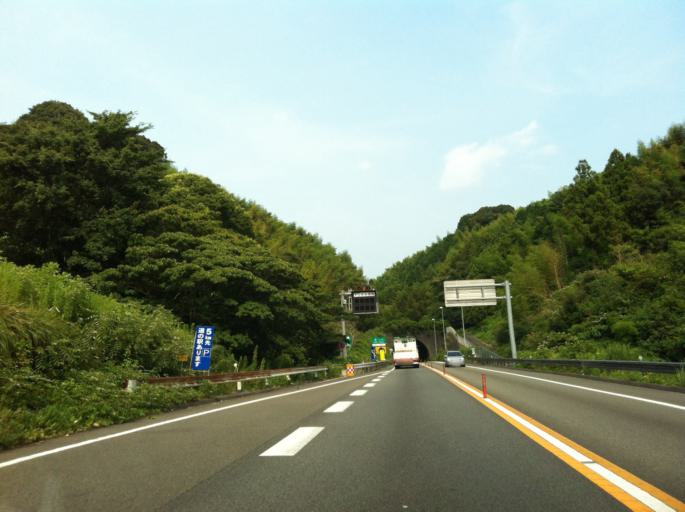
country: JP
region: Shizuoka
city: Fujieda
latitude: 34.8932
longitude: 138.2674
